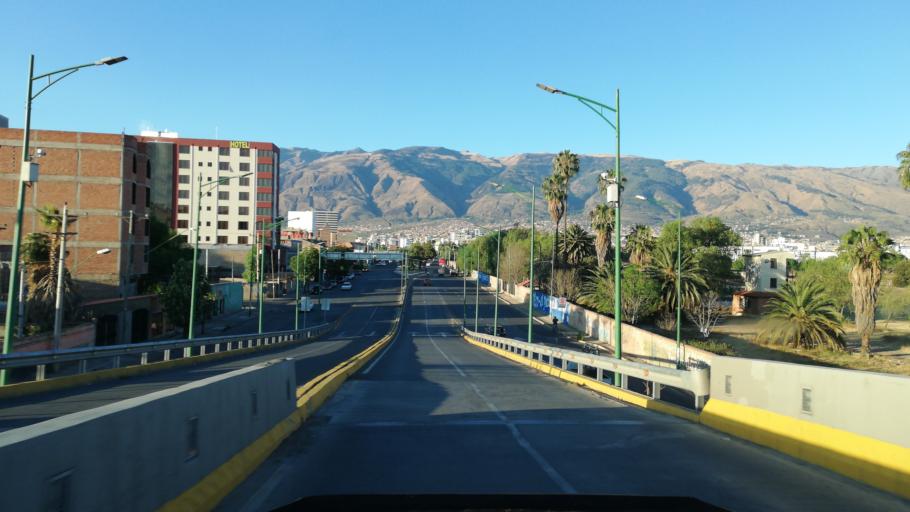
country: BO
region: Cochabamba
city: Cochabamba
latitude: -17.3916
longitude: -66.1838
